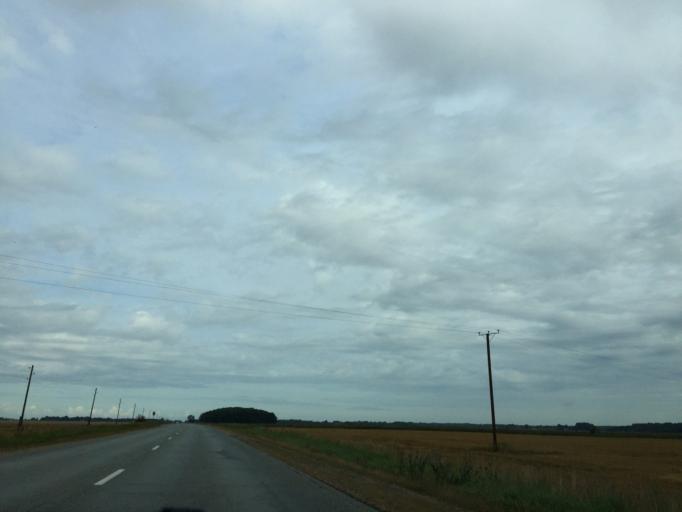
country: LV
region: Engure
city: Smarde
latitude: 56.7892
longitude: 23.3735
